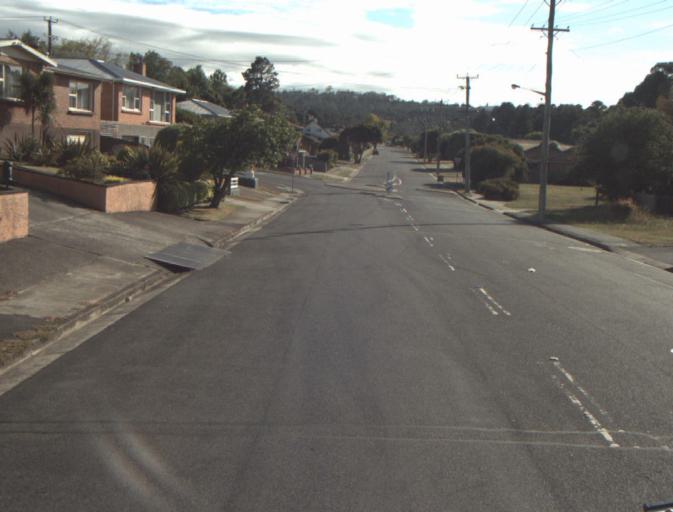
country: AU
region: Tasmania
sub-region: Launceston
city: Newnham
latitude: -41.3970
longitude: 147.1284
